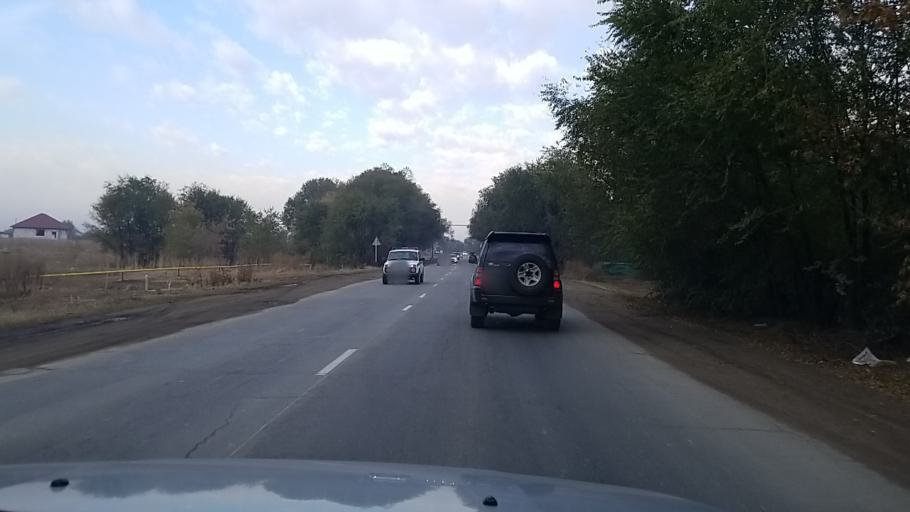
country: KZ
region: Almaty Oblysy
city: Burunday
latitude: 43.3597
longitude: 76.7524
